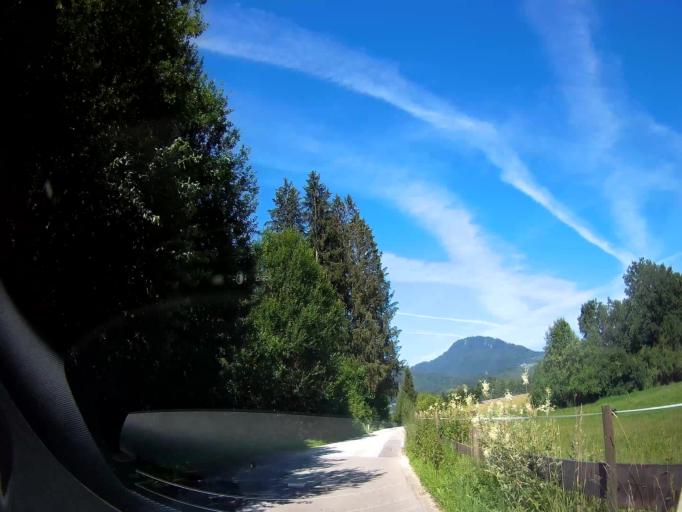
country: AT
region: Carinthia
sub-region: Politischer Bezirk Klagenfurt Land
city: Maria Saal
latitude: 46.6893
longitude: 14.3535
